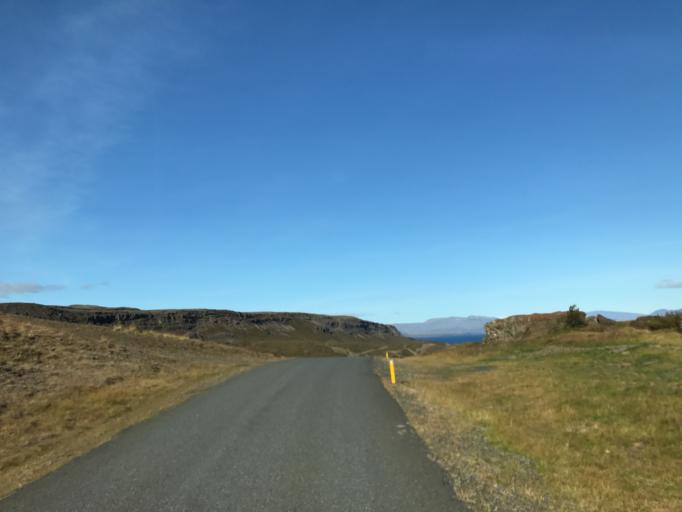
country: IS
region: South
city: Hveragerdi
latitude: 64.1457
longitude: -21.2599
